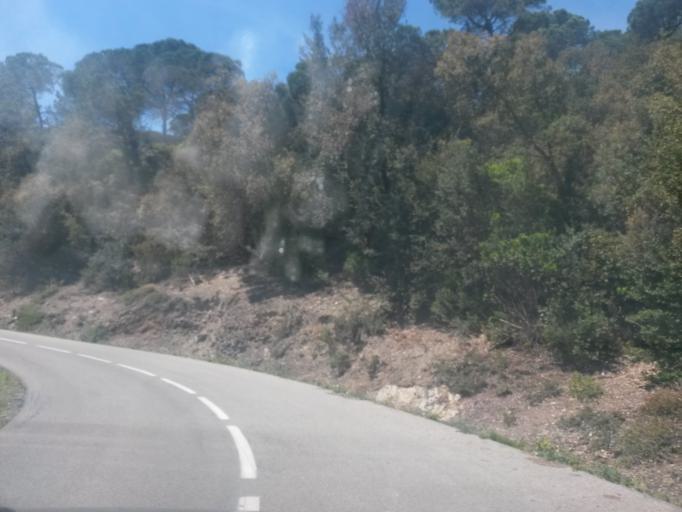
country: ES
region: Catalonia
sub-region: Provincia de Girona
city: Cassa de la Selva
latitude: 41.9224
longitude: 2.9145
